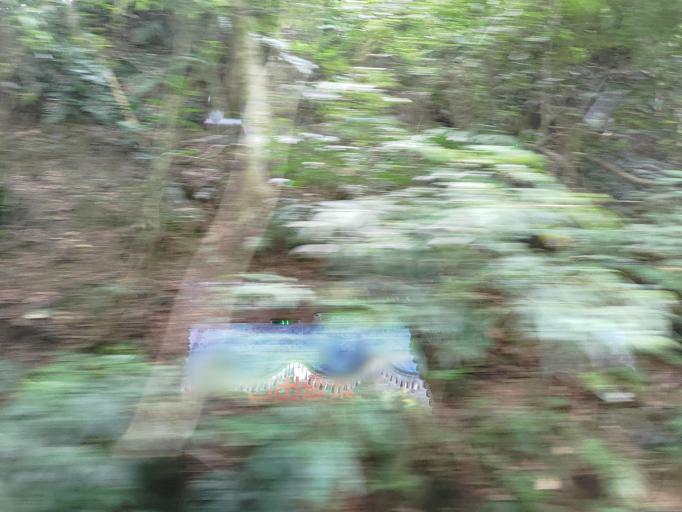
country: TW
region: Taiwan
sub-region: Hsinchu
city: Hsinchu
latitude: 24.6198
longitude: 121.0430
